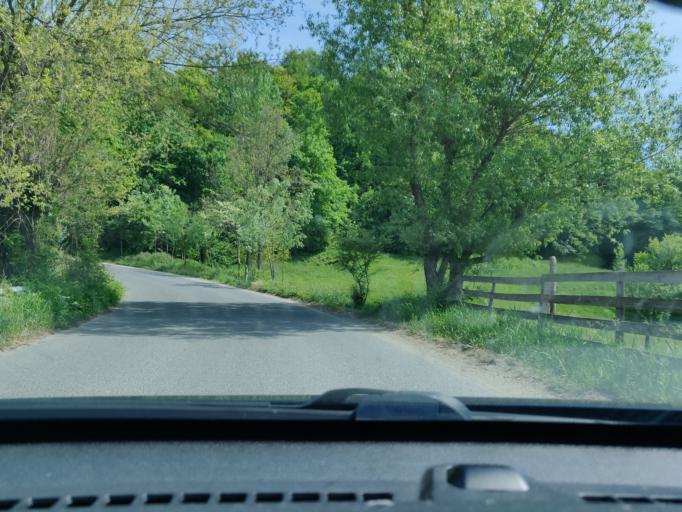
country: RO
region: Vrancea
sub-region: Comuna Vidra
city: Vidra
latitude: 45.9250
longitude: 26.8976
